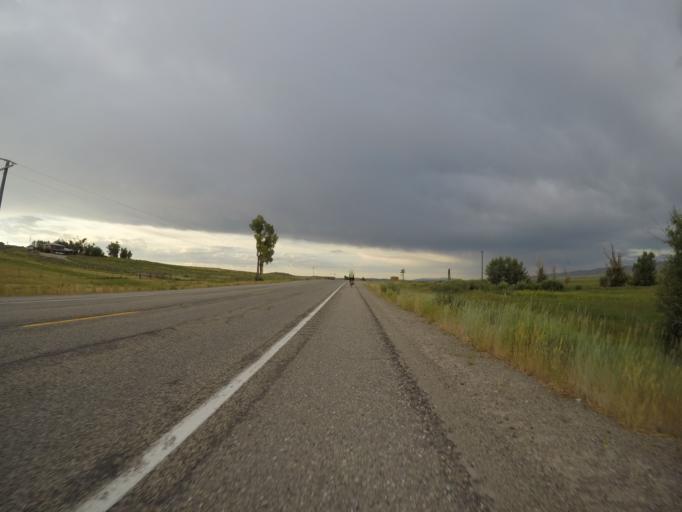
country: US
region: Idaho
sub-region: Bear Lake County
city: Montpelier
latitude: 42.0492
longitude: -110.9314
